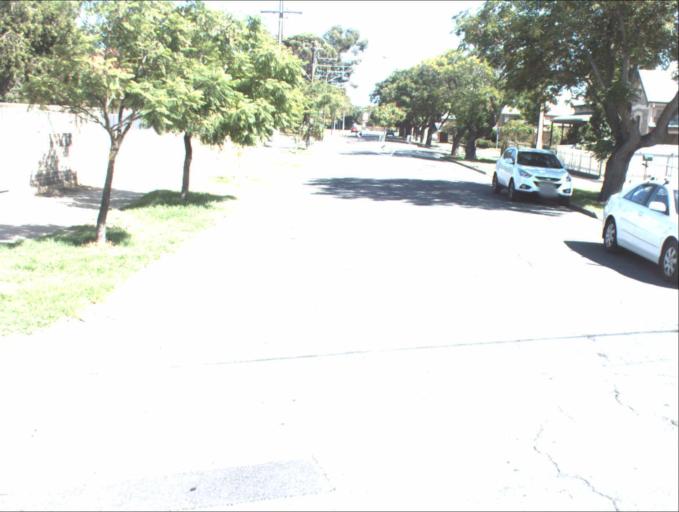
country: AU
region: South Australia
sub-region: Port Adelaide Enfield
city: Alberton
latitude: -34.8580
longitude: 138.5169
